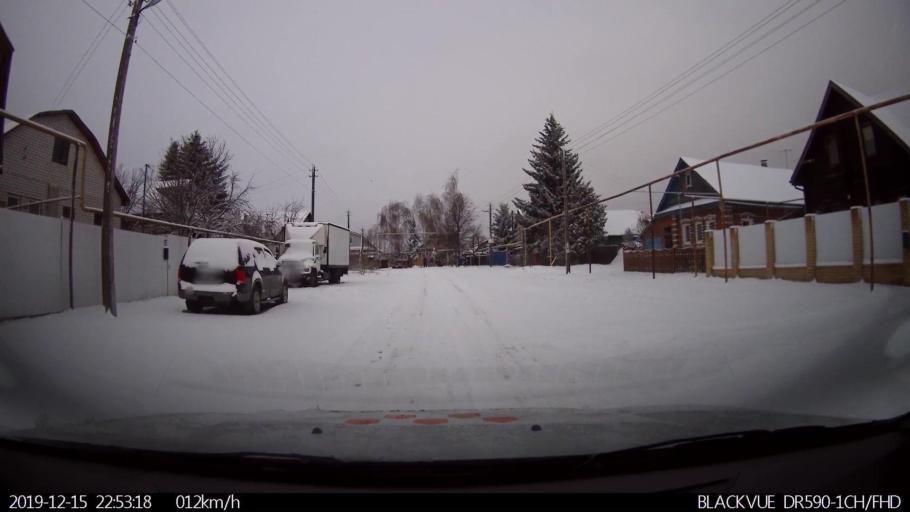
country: RU
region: Nizjnij Novgorod
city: Afonino
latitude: 56.2203
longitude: 44.1130
